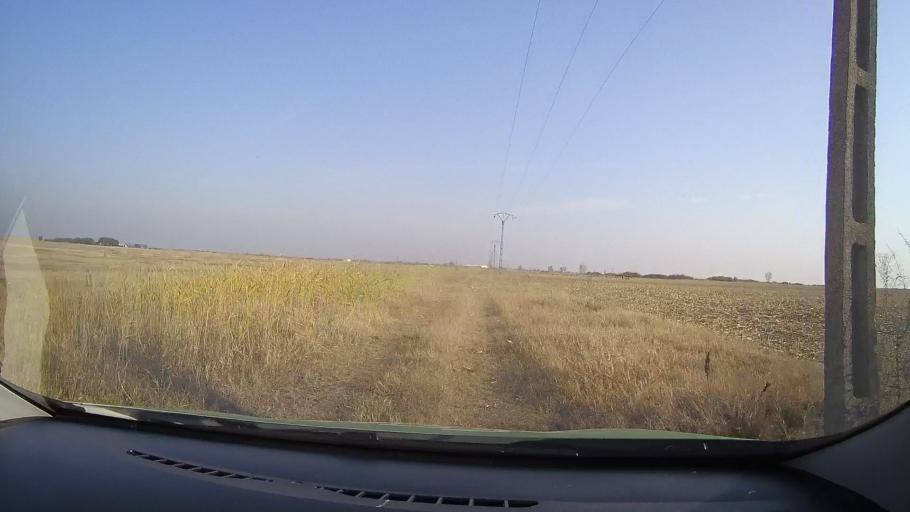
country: RO
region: Arad
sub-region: Comuna Pilu
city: Pilu
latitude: 46.5570
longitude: 21.3370
